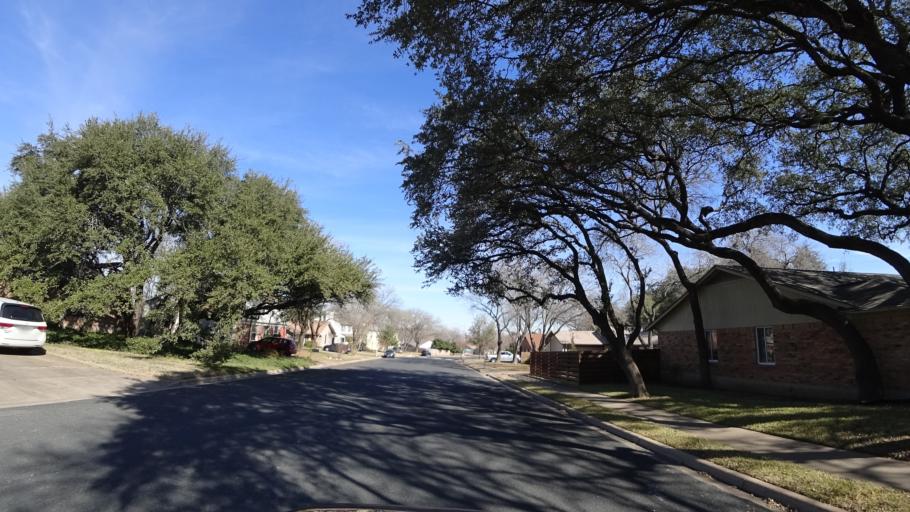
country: US
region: Texas
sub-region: Travis County
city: Wells Branch
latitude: 30.3892
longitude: -97.6922
